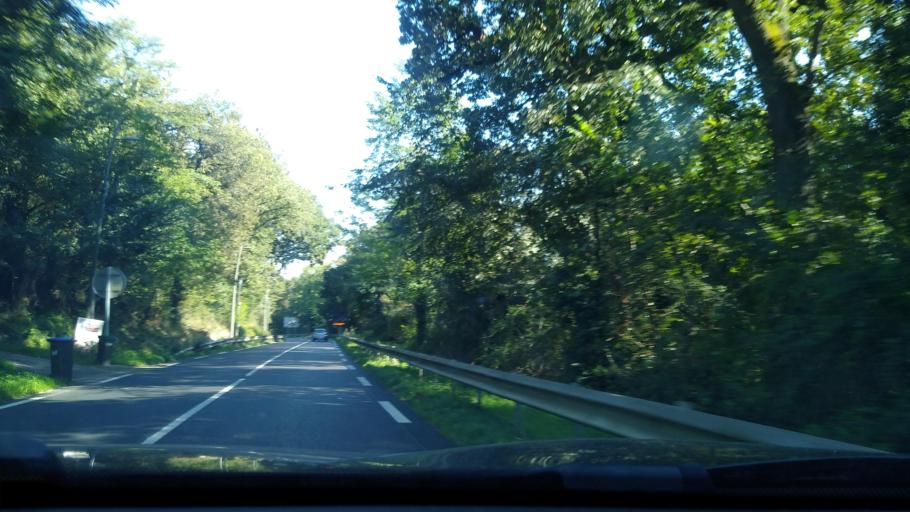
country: FR
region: Midi-Pyrenees
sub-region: Departement de la Haute-Garonne
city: Mondonville
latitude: 43.6722
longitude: 1.2894
